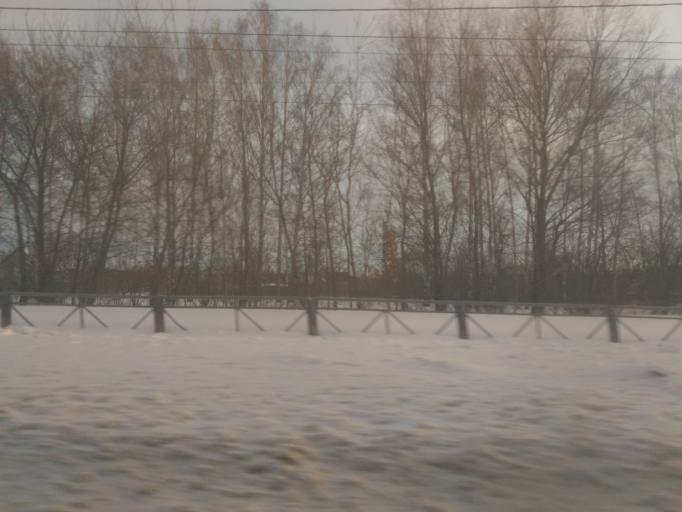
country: RU
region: Ulyanovsk
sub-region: Ulyanovskiy Rayon
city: Ulyanovsk
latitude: 54.3645
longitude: 48.3295
